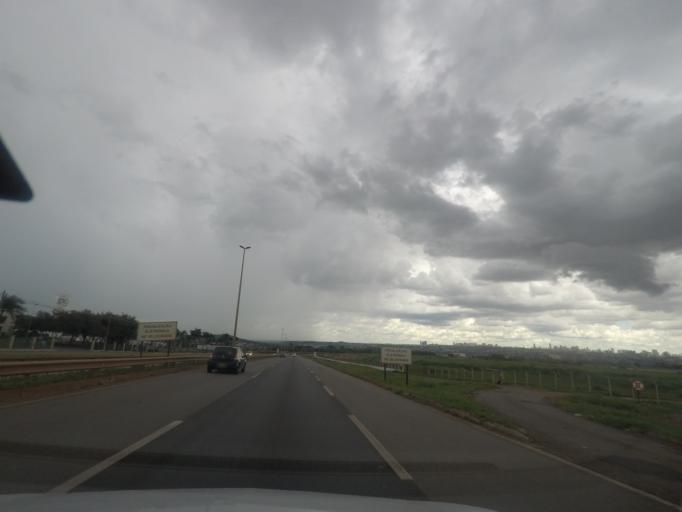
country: BR
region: Goias
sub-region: Goiania
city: Goiania
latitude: -16.6309
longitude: -49.2055
